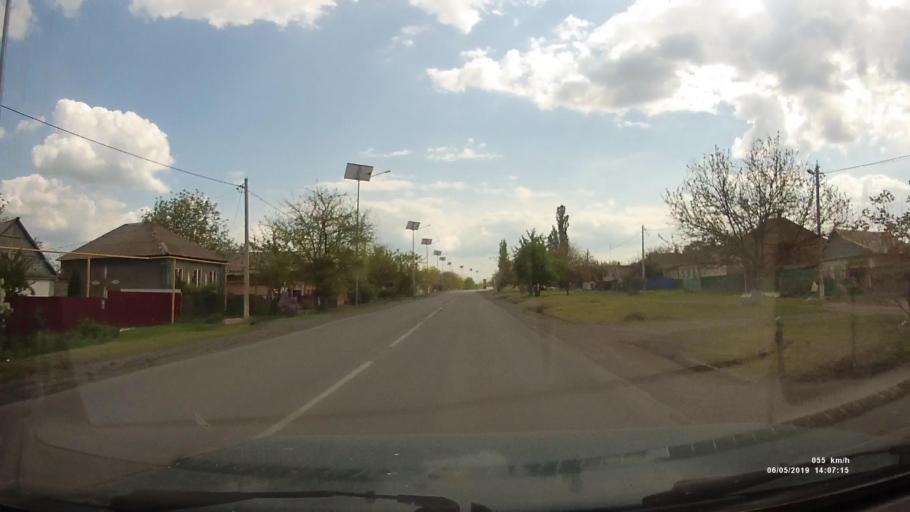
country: RU
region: Rostov
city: Shakhty
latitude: 47.6824
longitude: 40.3032
